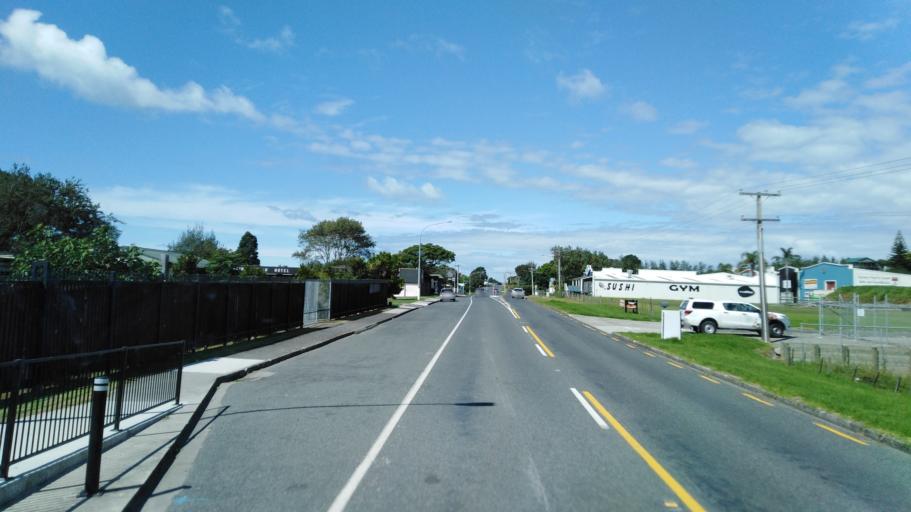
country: NZ
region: Bay of Plenty
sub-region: Western Bay of Plenty District
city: Waihi Beach
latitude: -37.4086
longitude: 175.9370
